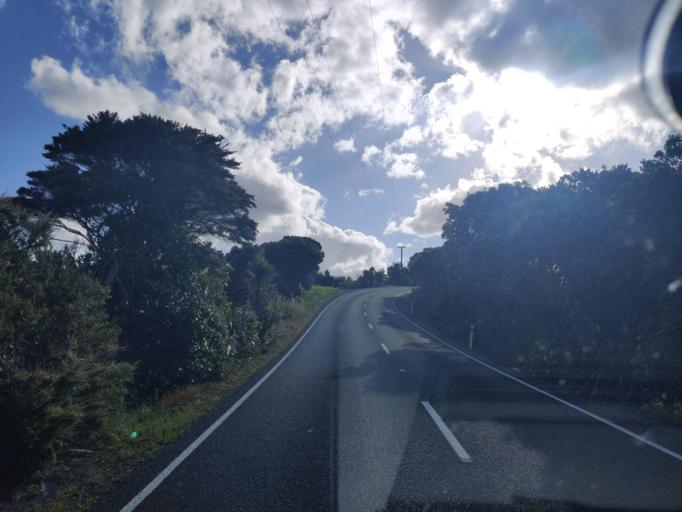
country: NZ
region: Northland
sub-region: Whangarei
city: Ngunguru
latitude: -35.6168
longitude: 174.5251
